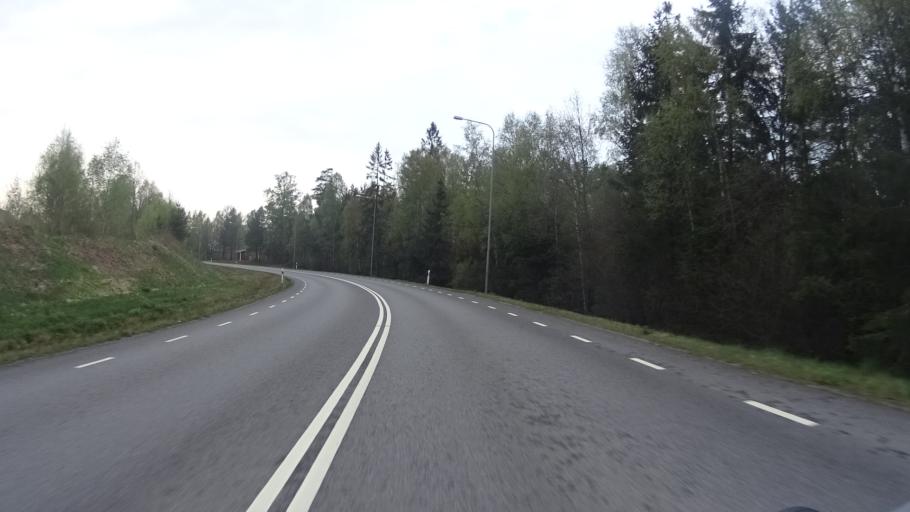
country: SE
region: Kronoberg
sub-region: Ljungby Kommun
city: Ljungby
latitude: 56.8313
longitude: 13.9746
